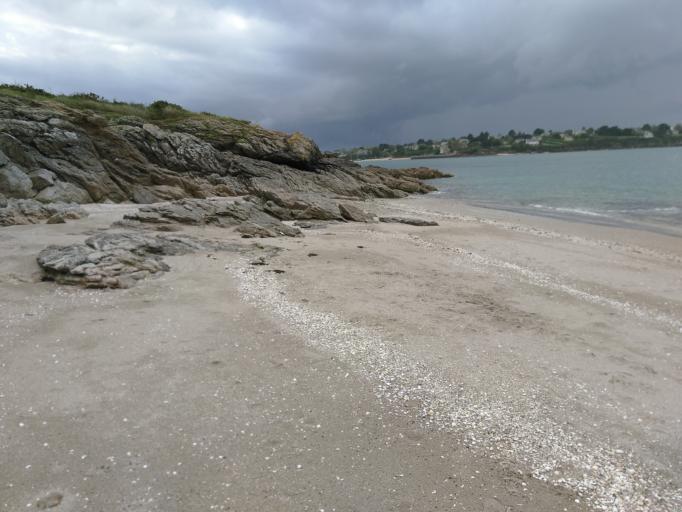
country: FR
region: Brittany
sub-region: Departement des Cotes-d'Armor
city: Lancieux
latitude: 48.5964
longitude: -2.1709
